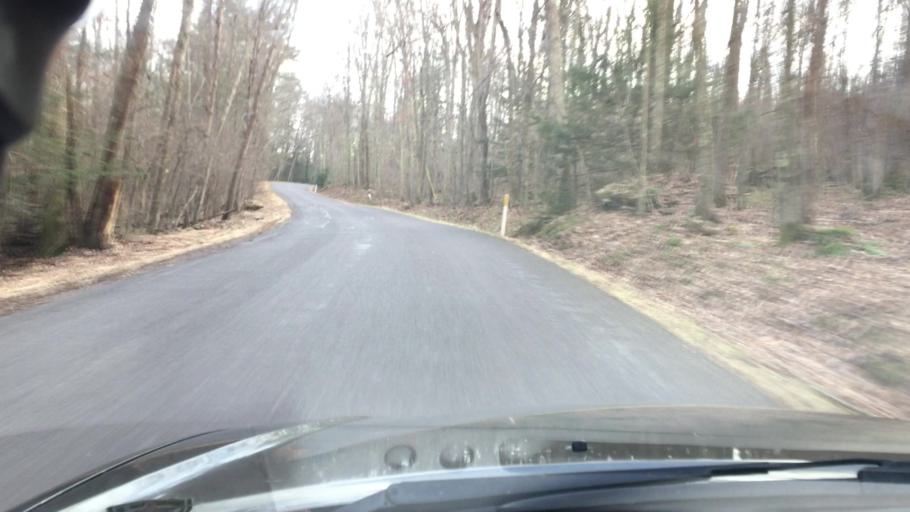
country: US
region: Pennsylvania
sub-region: Luzerne County
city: Back Mountain
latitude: 41.3012
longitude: -76.0481
